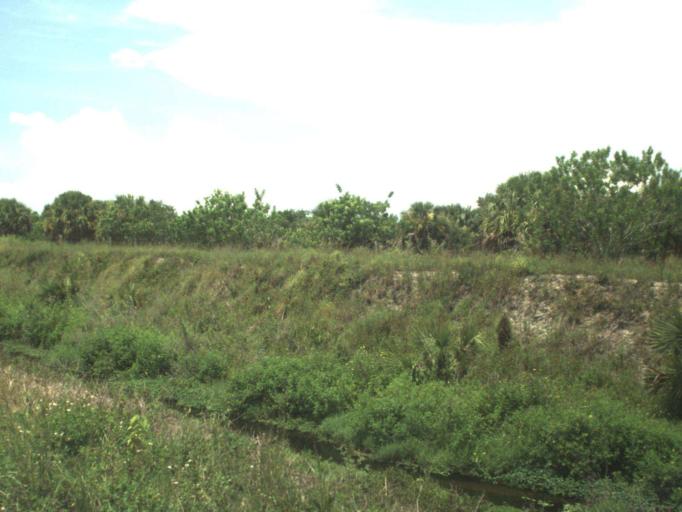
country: US
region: Florida
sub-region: Saint Lucie County
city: Lakewood Park
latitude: 27.5208
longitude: -80.4150
